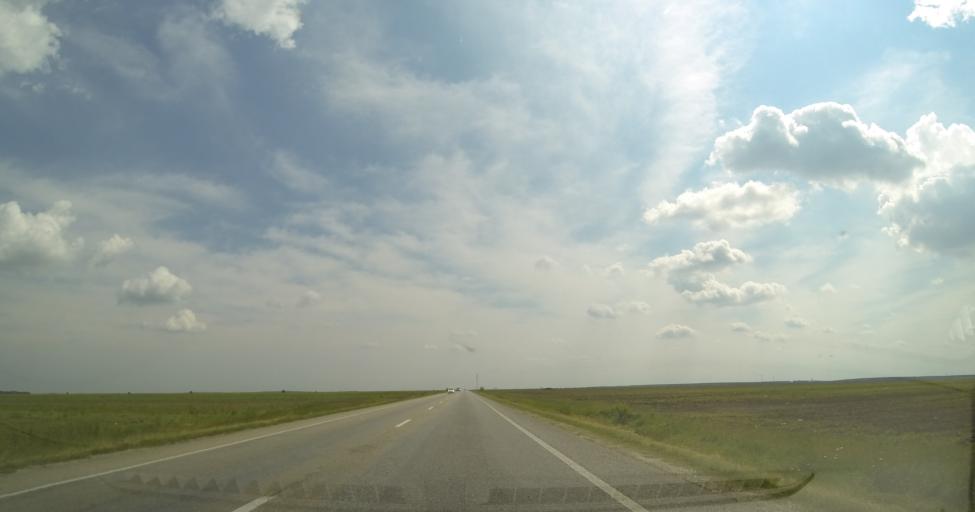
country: RO
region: Olt
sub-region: Comuna Scornicesti
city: Negreni
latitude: 44.5867
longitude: 24.6056
